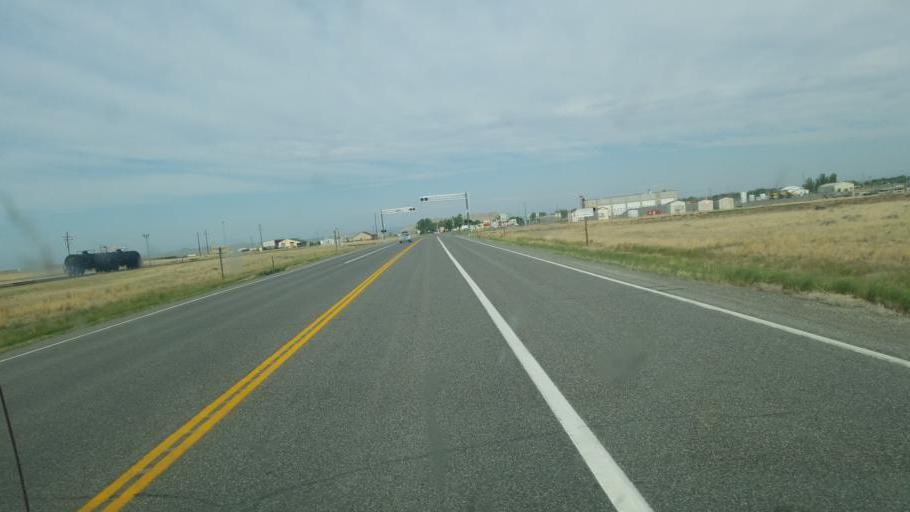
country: US
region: Wyoming
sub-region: Fremont County
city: Riverton
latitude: 43.2362
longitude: -108.0959
